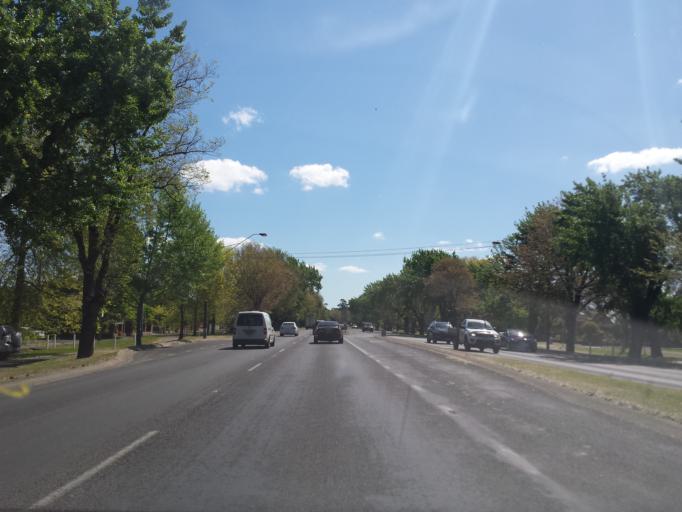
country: AU
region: Victoria
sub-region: Ballarat North
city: Newington
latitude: -37.5588
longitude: 143.8305
